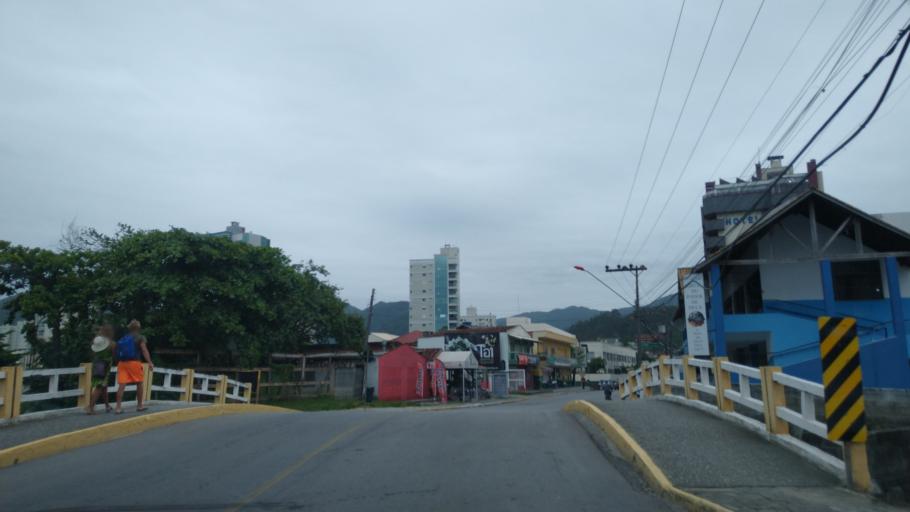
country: BR
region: Santa Catarina
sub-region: Itapema
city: Itapema
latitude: -27.0913
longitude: -48.6098
